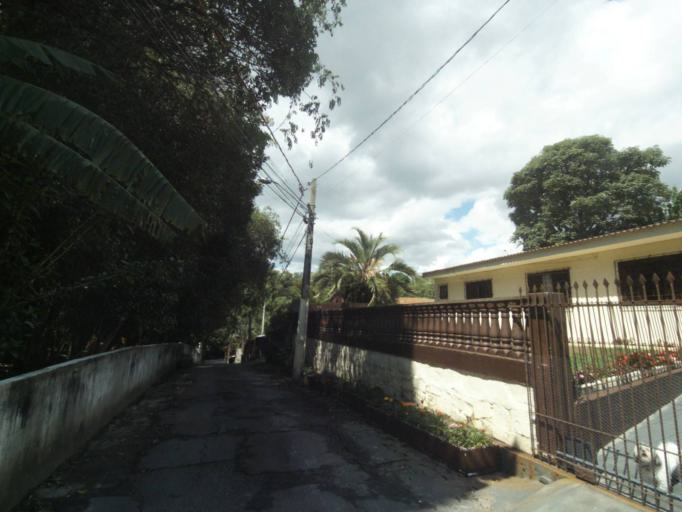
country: BR
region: Parana
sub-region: Curitiba
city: Curitiba
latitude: -25.4347
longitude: -49.3332
